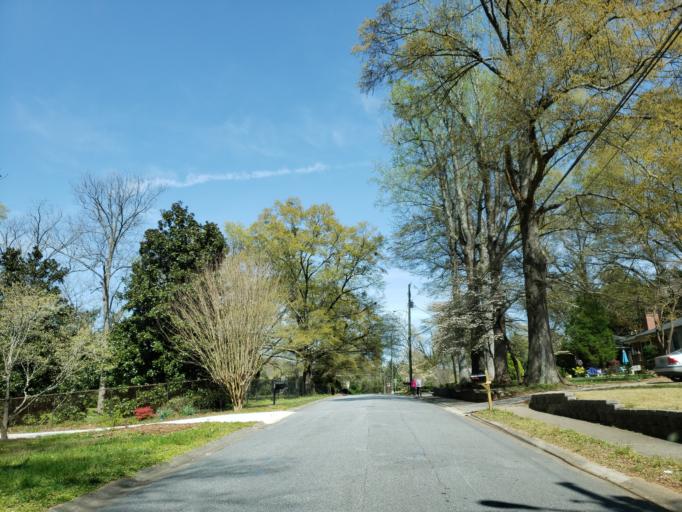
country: US
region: Georgia
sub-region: Cobb County
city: Marietta
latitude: 33.9612
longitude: -84.5571
